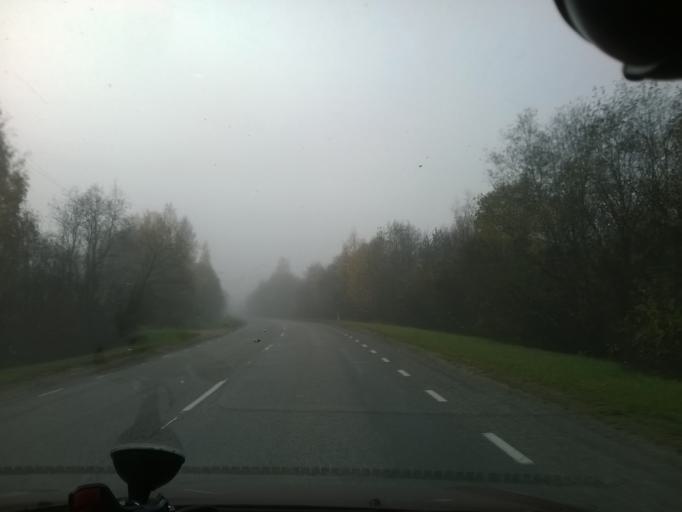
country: EE
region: Tartu
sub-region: Noo vald
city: Noo
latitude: 58.1513
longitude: 26.5269
